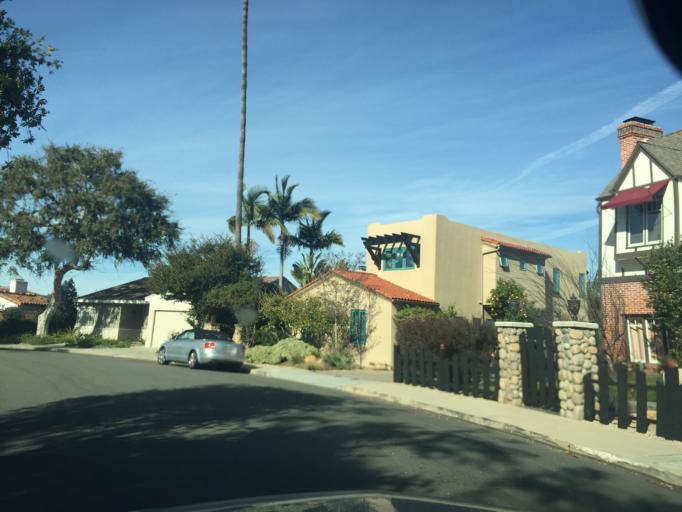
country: US
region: California
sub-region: San Diego County
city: Lemon Grove
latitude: 32.7673
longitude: -117.1008
